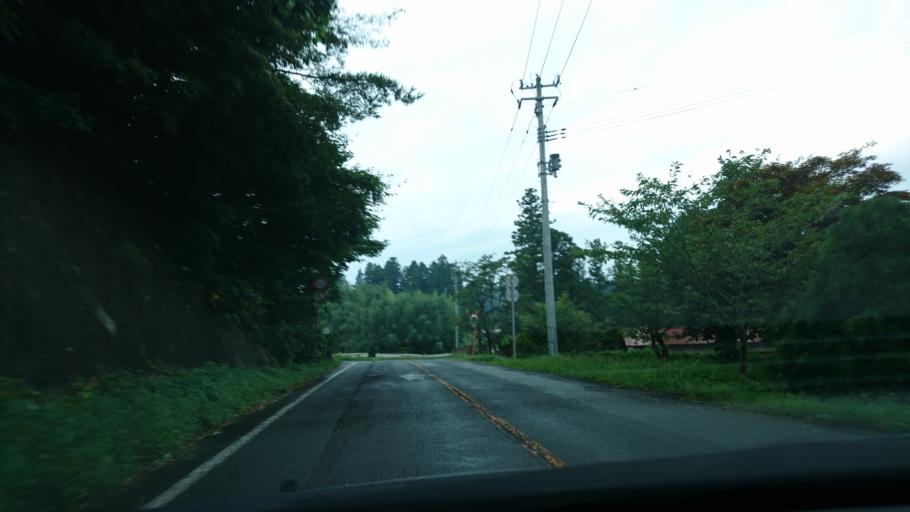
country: JP
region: Iwate
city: Ichinoseki
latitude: 39.0214
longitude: 141.2055
